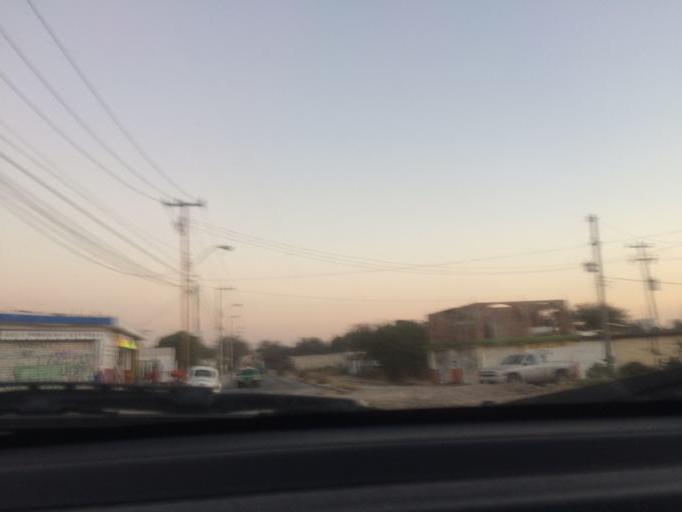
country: MX
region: Guanajuato
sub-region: Leon
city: Fraccionamiento Paraiso Real
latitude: 21.1197
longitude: -101.5899
